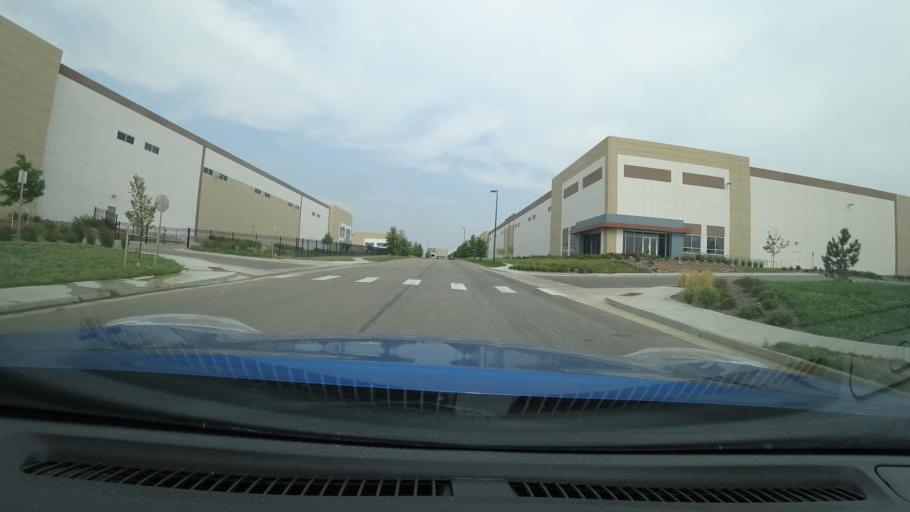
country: US
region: Colorado
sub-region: Adams County
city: Aurora
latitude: 39.7487
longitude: -104.7606
